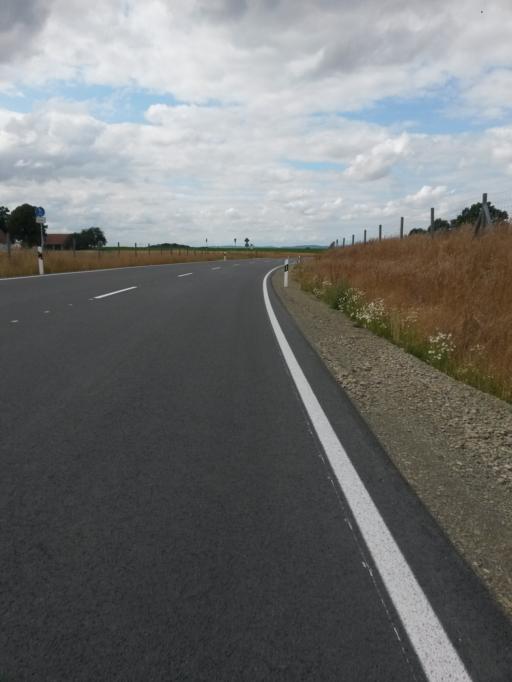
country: DE
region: North Rhine-Westphalia
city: Loehne
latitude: 52.1649
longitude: 8.7517
